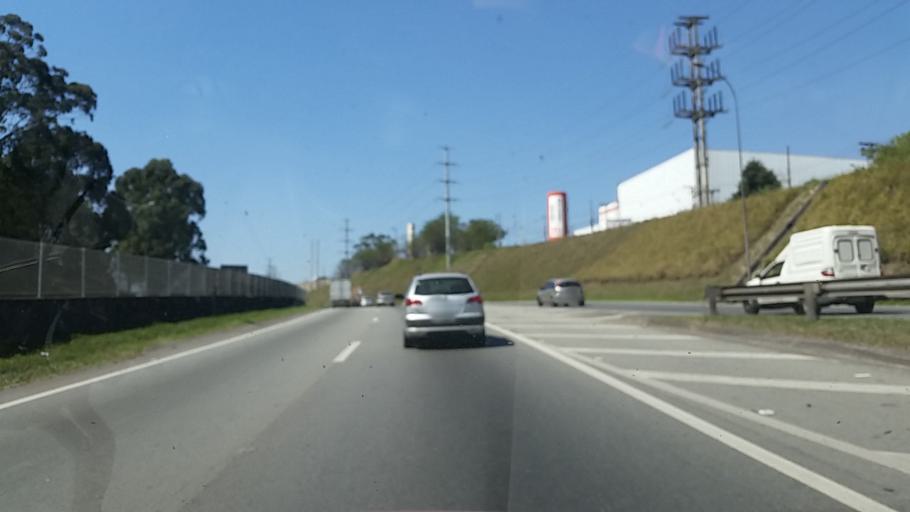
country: BR
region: Sao Paulo
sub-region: Embu
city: Embu
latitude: -23.6356
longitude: -46.8263
